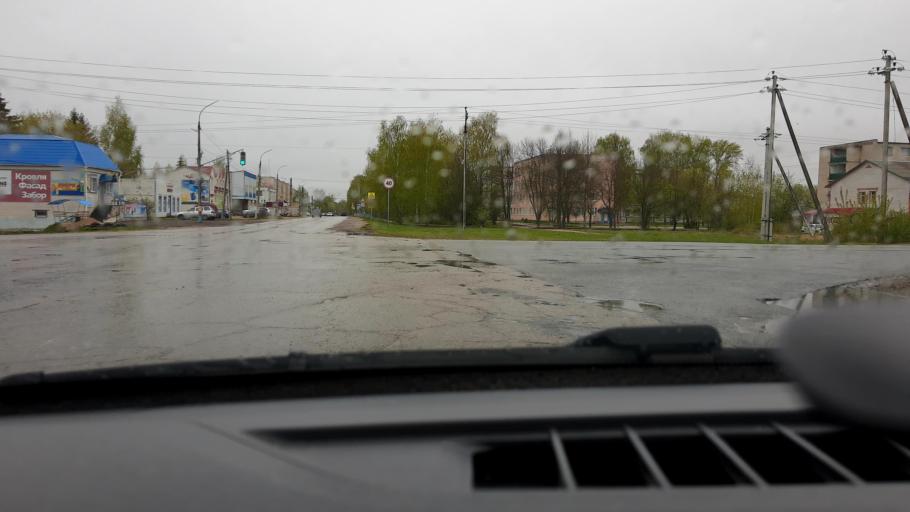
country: RU
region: Nizjnij Novgorod
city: Perevoz
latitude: 55.5979
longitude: 44.5616
